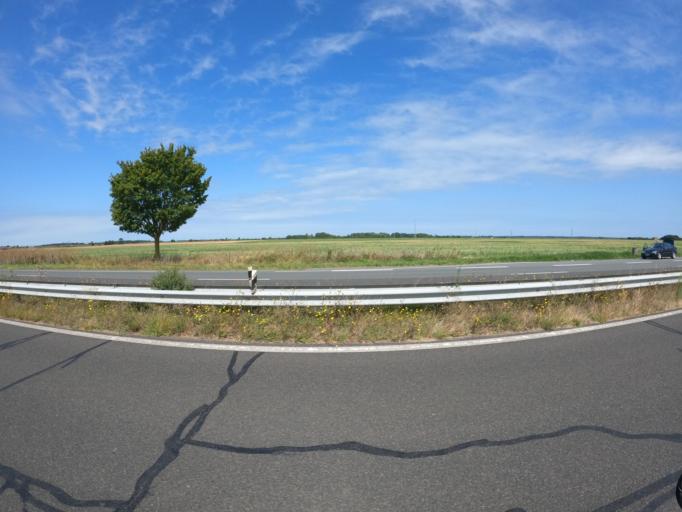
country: FR
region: Poitou-Charentes
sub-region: Departement des Deux-Sevres
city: Frontenay-Rohan-Rohan
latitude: 46.2472
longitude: -0.5632
